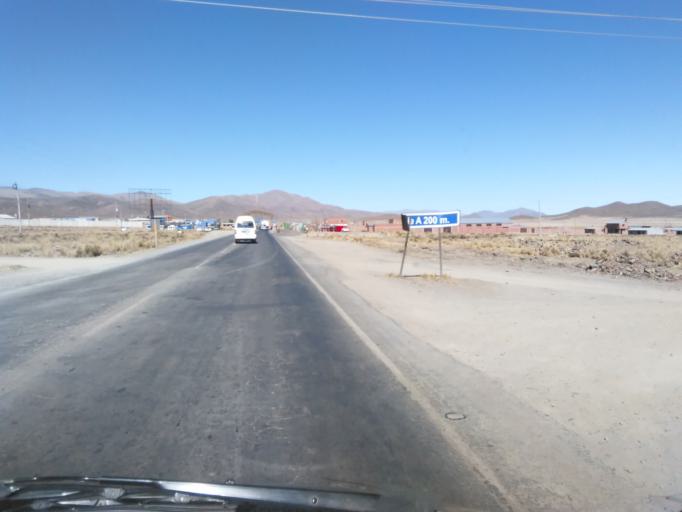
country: BO
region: Oruro
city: Oruro
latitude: -18.0167
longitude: -67.0323
